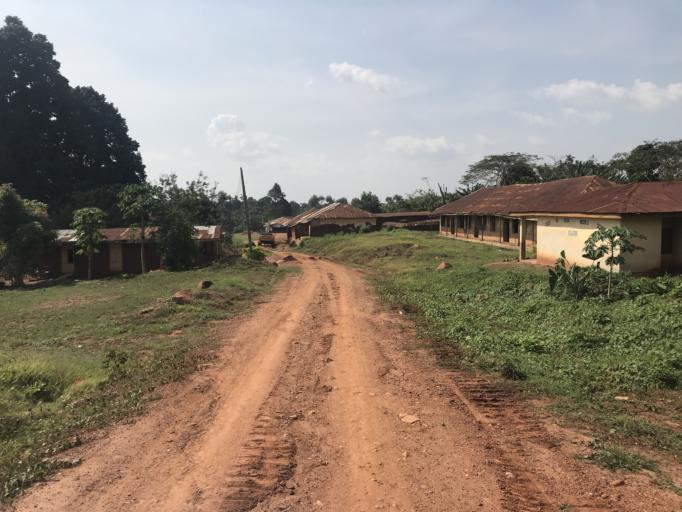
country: NG
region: Osun
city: Ilesa
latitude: 7.6353
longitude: 4.6728
